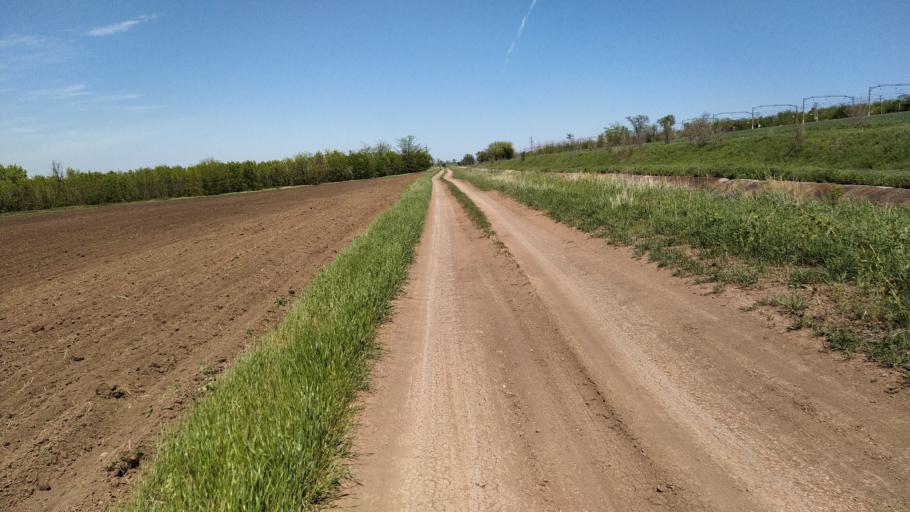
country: RU
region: Rostov
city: Kuleshovka
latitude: 47.0334
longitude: 39.6359
